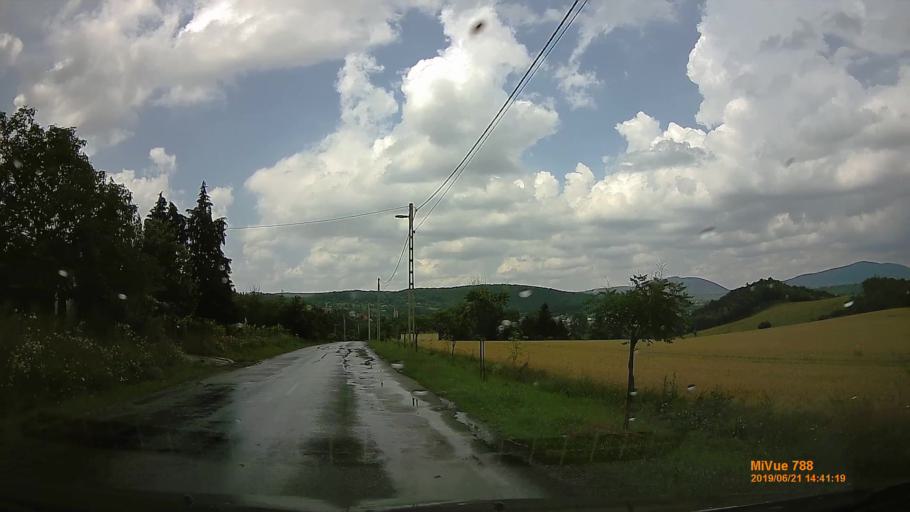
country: HU
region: Baranya
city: Hosszuheteny
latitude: 46.1149
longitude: 18.3123
